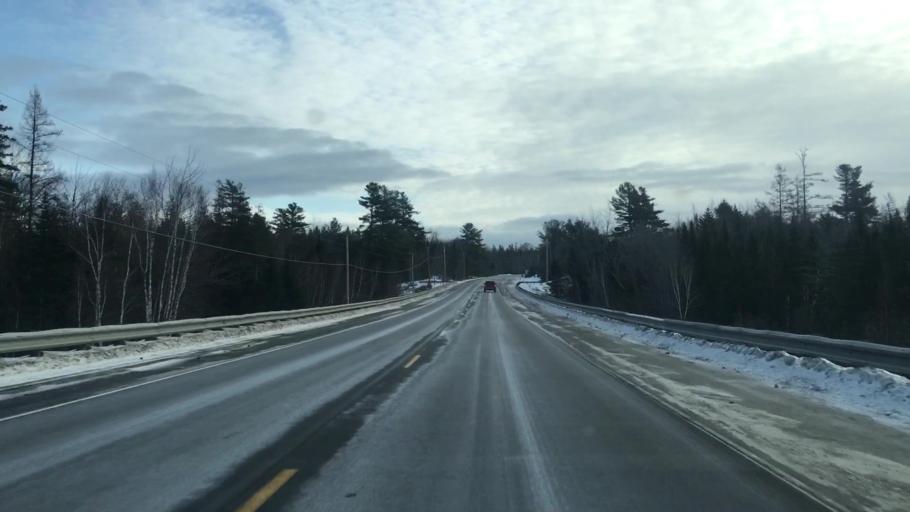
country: US
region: Maine
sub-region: Washington County
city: Machias
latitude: 44.9503
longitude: -67.6781
